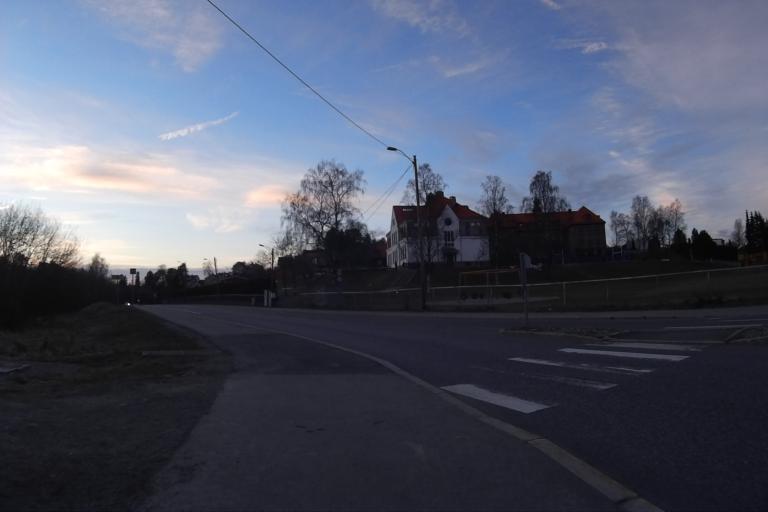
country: NO
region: Oslo
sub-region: Oslo
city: Oslo
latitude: 59.8983
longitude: 10.8310
